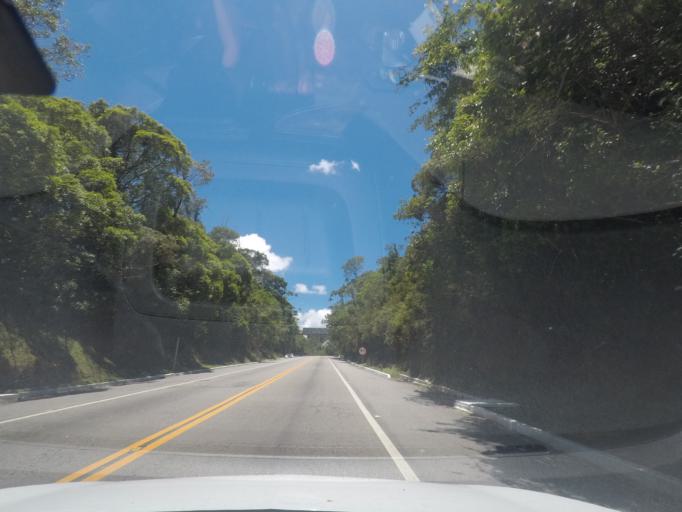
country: BR
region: Rio de Janeiro
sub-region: Teresopolis
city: Teresopolis
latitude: -22.4618
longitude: -42.9841
